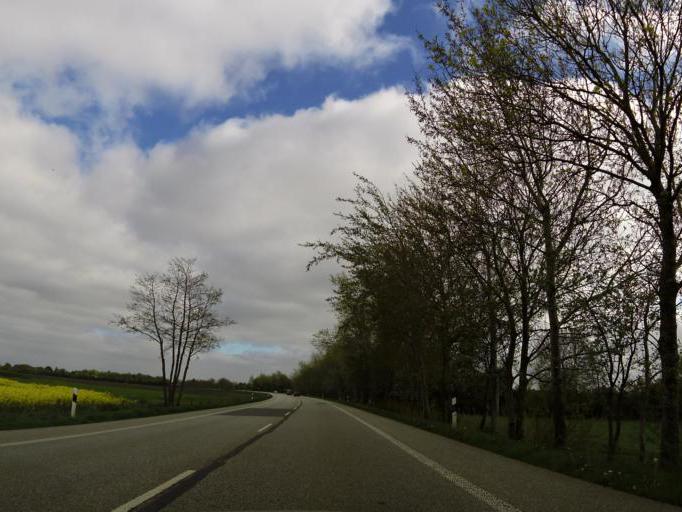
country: DE
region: Schleswig-Holstein
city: Risum-Lindholm
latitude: 54.7755
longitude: 8.8562
